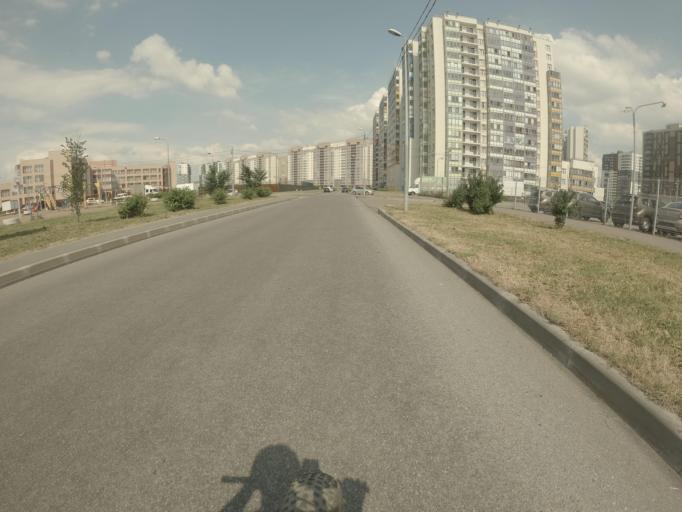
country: RU
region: St.-Petersburg
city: Krasnogvargeisky
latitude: 59.9150
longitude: 30.4363
